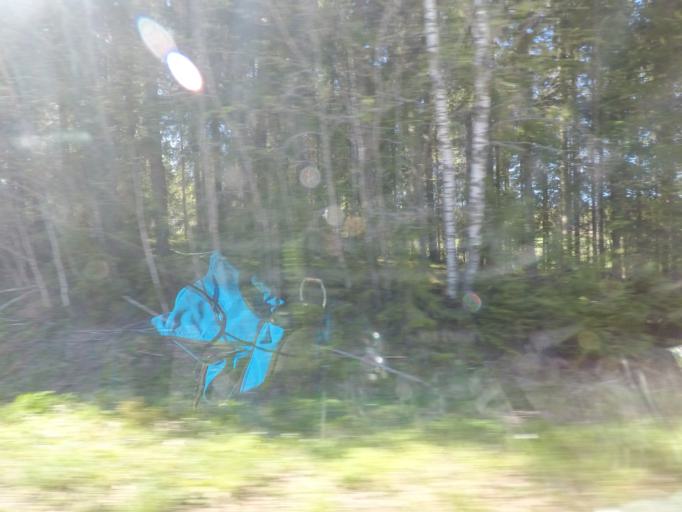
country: FI
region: Uusimaa
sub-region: Helsinki
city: Sammatti
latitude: 60.4028
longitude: 23.8183
